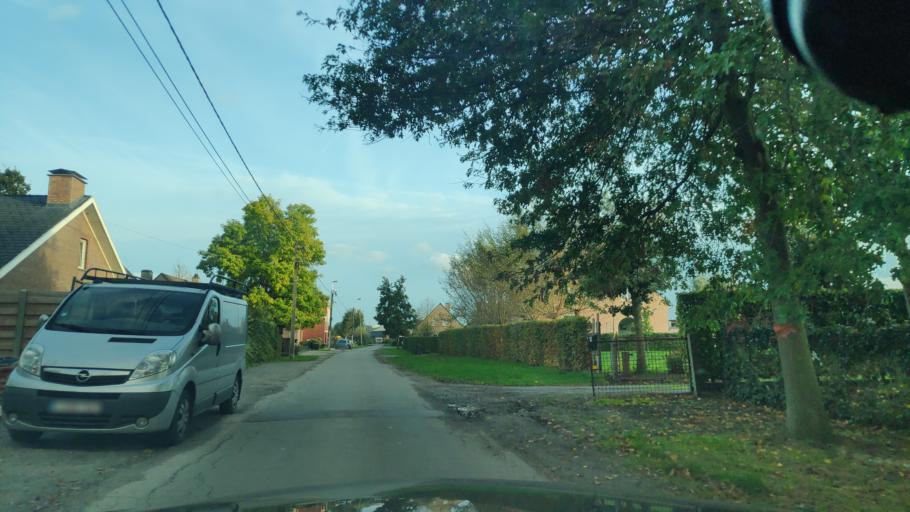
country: BE
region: Flanders
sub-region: Provincie Oost-Vlaanderen
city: Aalter
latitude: 51.1177
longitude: 3.4462
